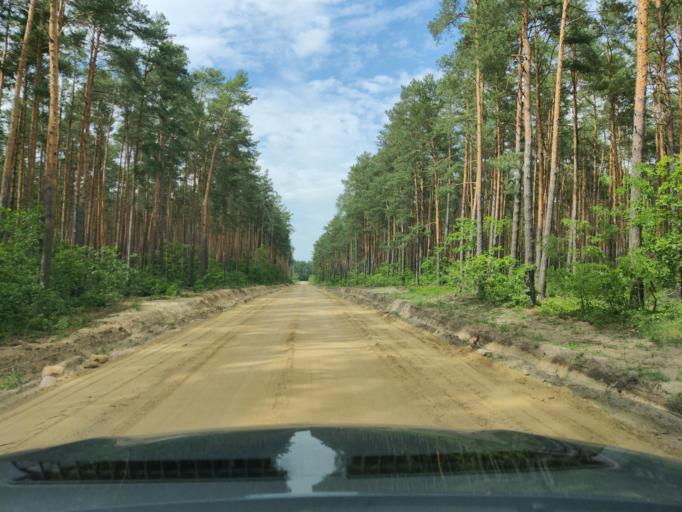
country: PL
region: Masovian Voivodeship
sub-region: Powiat pultuski
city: Pultusk
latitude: 52.7148
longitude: 21.1507
